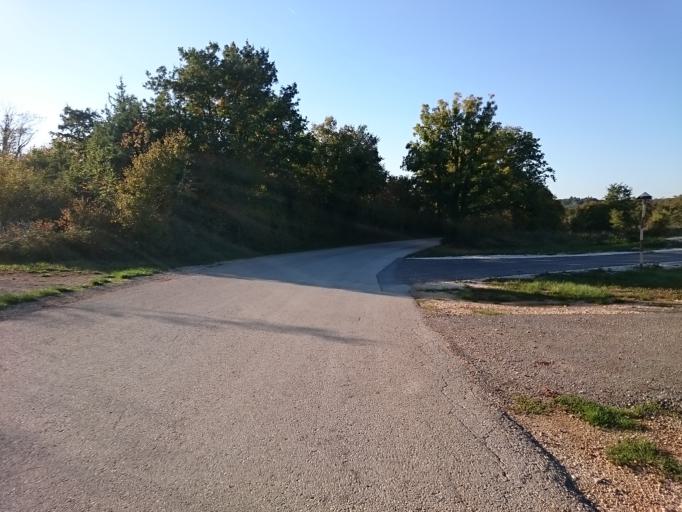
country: HR
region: Istarska
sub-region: Grad Porec
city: Porec
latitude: 45.2908
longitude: 13.6400
